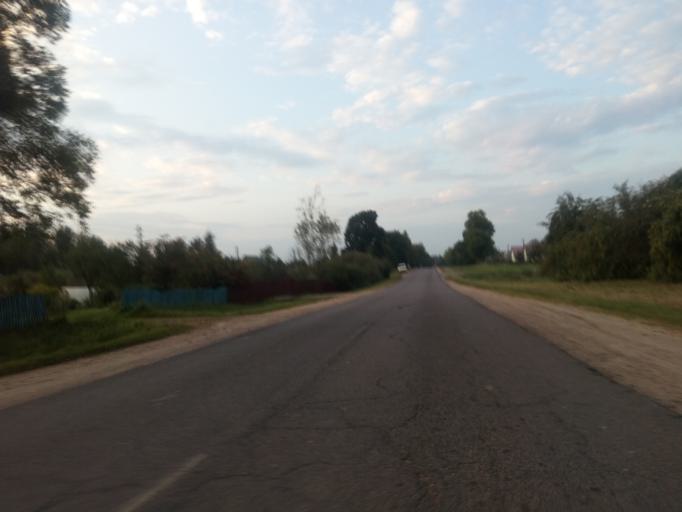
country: BY
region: Vitebsk
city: Dzisna
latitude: 55.6583
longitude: 28.3235
